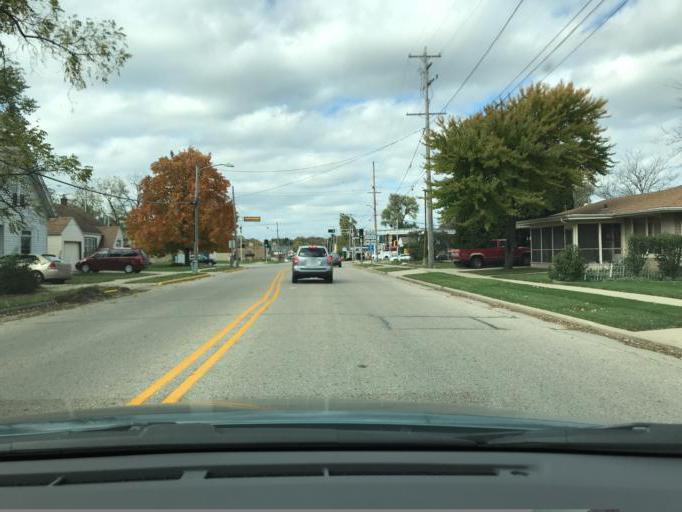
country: US
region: Wisconsin
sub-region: Racine County
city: Burlington
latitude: 42.6776
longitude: -88.2689
